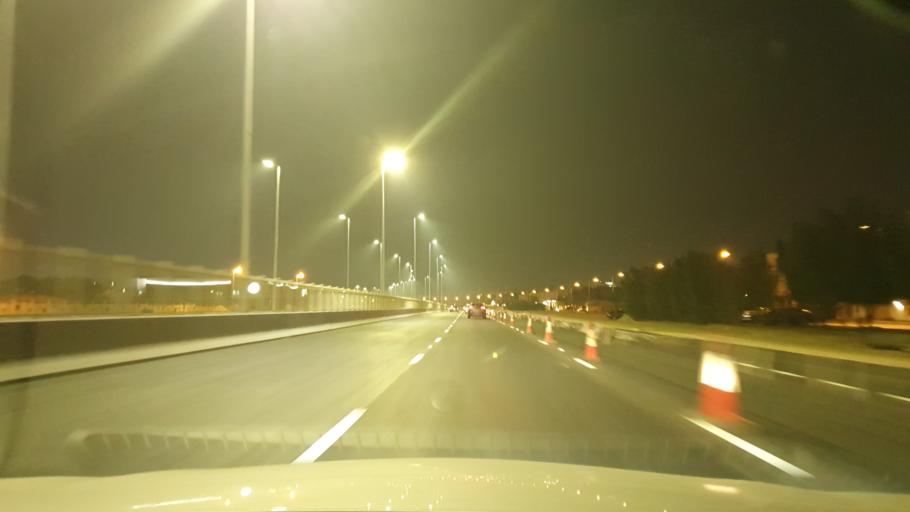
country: BH
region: Northern
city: Madinat `Isa
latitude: 26.1573
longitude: 50.5503
